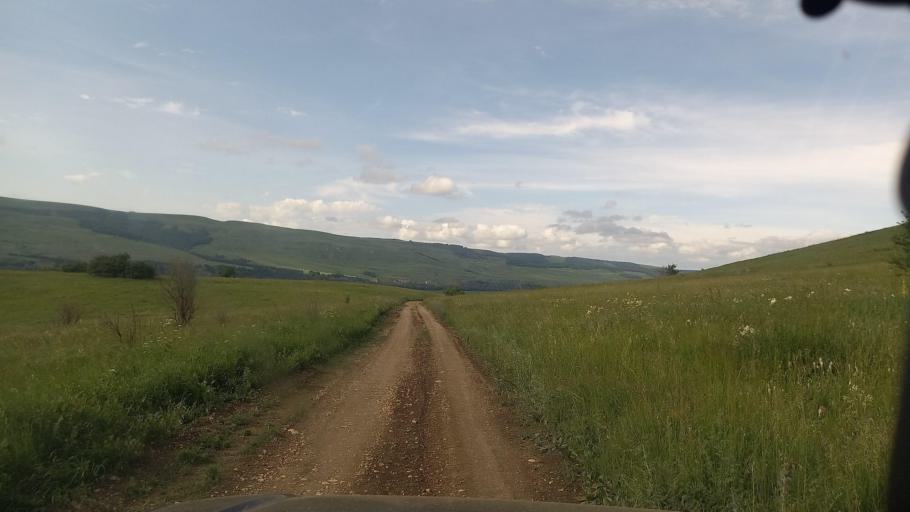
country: RU
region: Krasnodarskiy
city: Peredovaya
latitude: 44.0785
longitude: 41.3641
